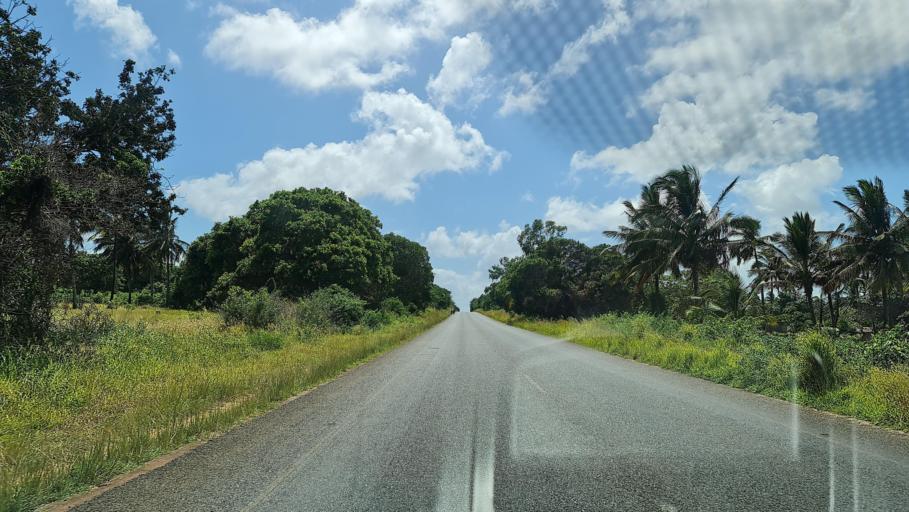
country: MZ
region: Inhambane
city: Maxixe
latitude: -24.5365
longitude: 34.9397
